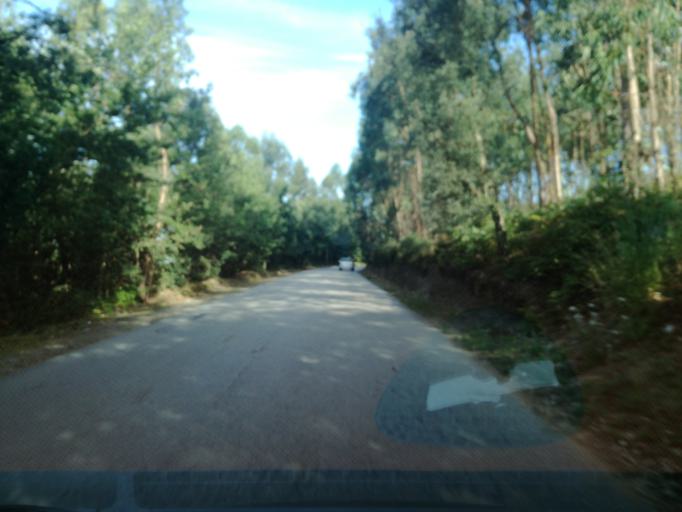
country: PT
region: Porto
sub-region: Valongo
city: Alfena
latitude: 41.2689
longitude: -8.5307
